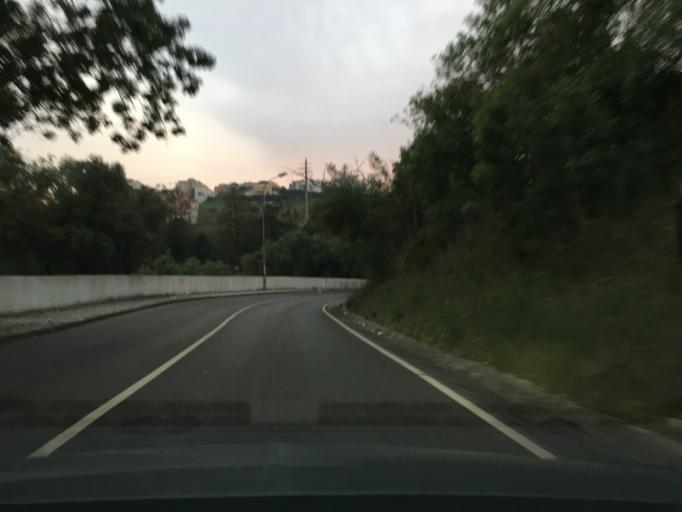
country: PT
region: Lisbon
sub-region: Oeiras
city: Carnaxide
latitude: 38.7231
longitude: -9.2486
